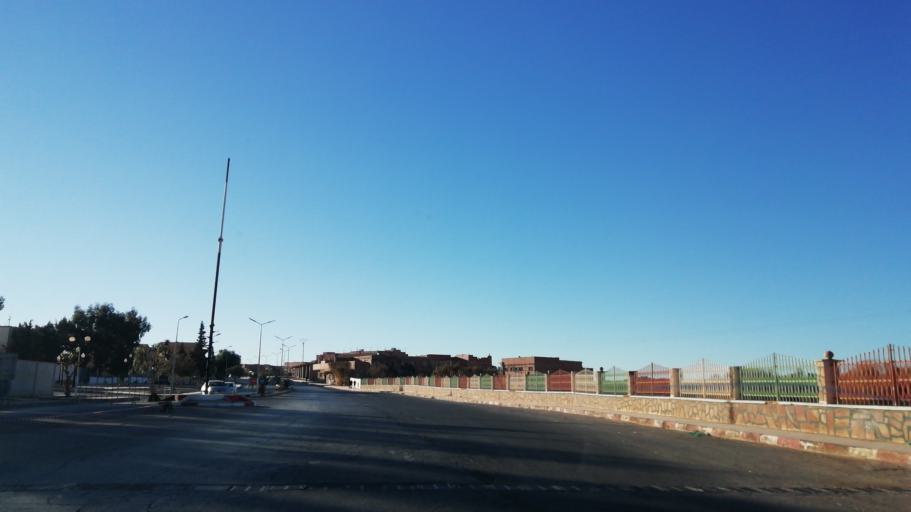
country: DZ
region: Saida
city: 'Ain el Hadjar
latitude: 34.0358
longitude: 0.0873
